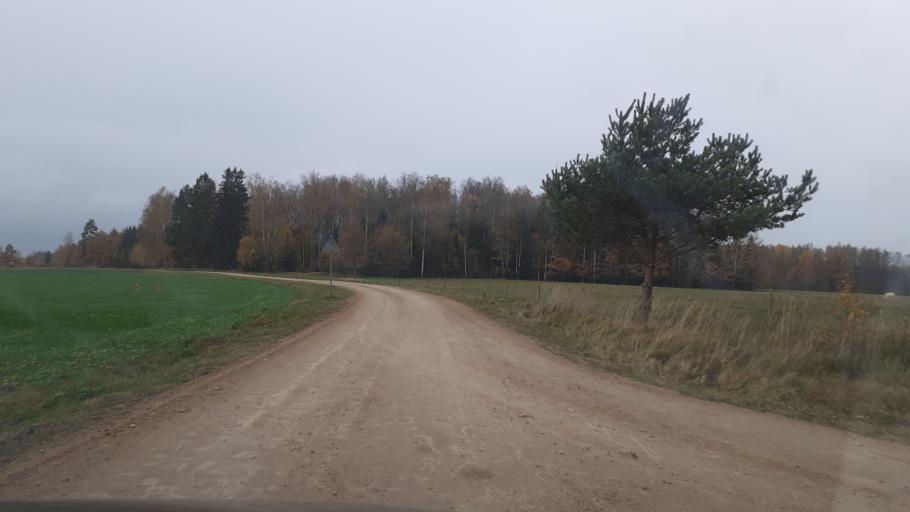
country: LV
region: Saldus Rajons
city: Saldus
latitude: 56.8719
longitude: 22.3301
